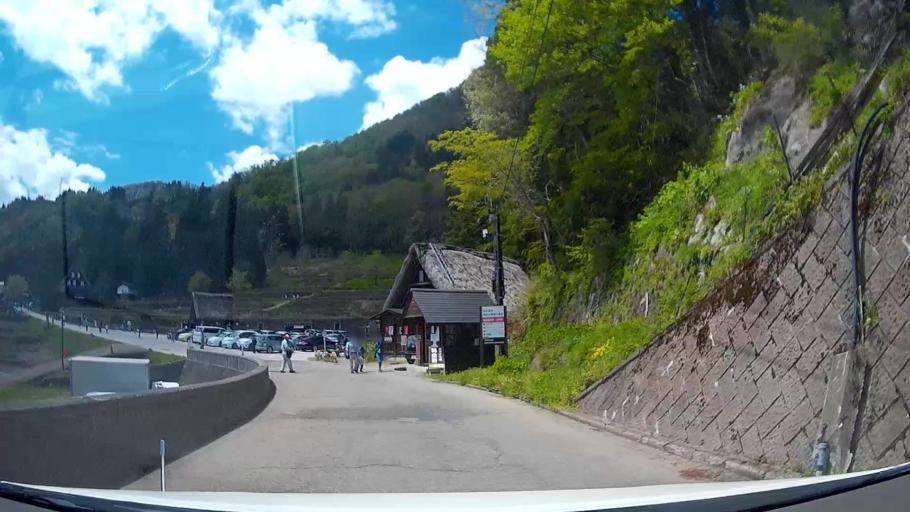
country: JP
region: Toyama
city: Nanto-shi
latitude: 36.4277
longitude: 136.9371
